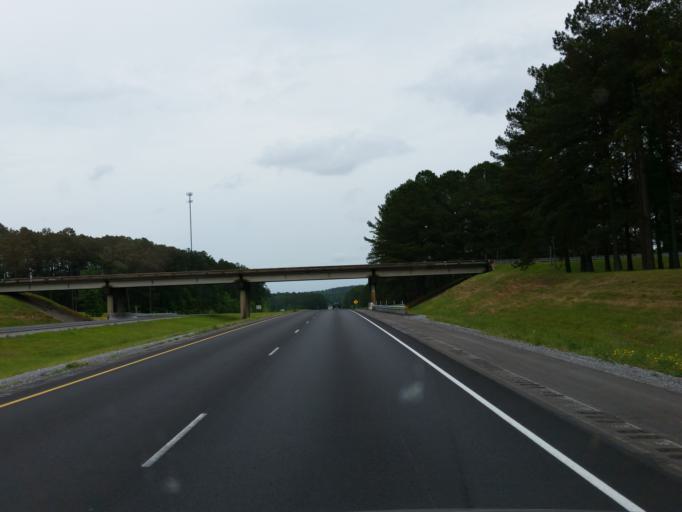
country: US
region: Mississippi
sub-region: Jones County
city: Sharon
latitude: 31.9638
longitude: -88.9682
